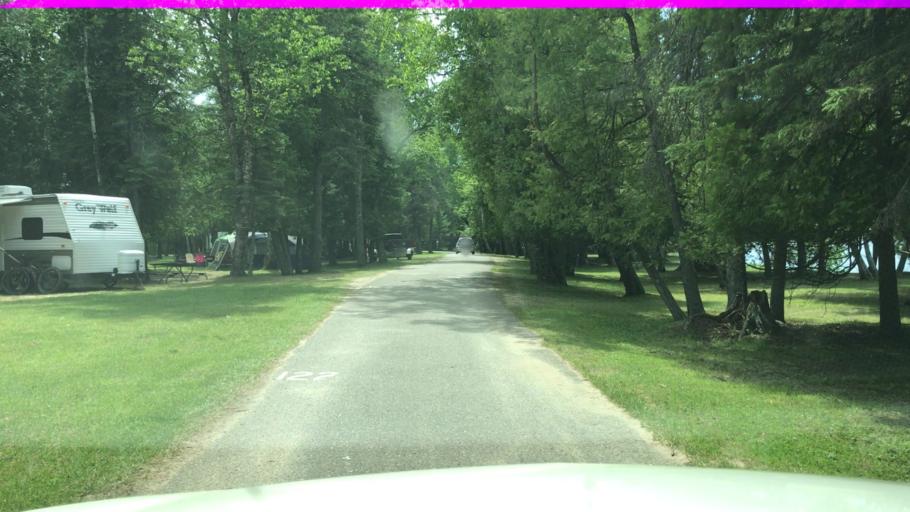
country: US
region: Michigan
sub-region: Schoolcraft County
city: Manistique
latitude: 45.9454
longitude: -86.3311
